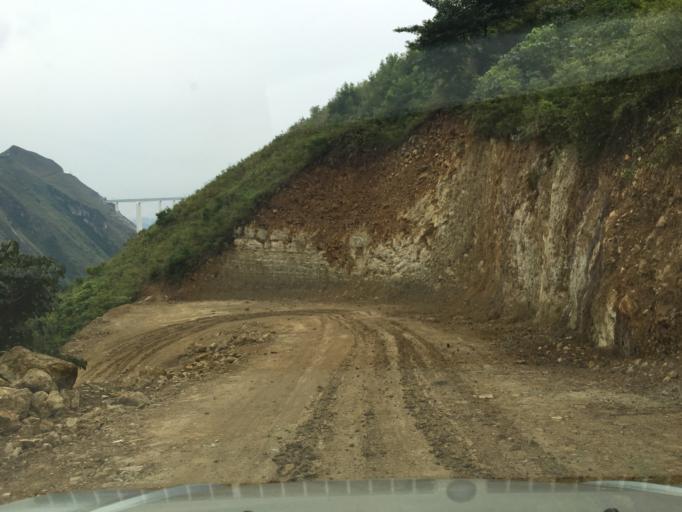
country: CN
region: Guizhou Sheng
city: Anshun
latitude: 25.9619
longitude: 105.2422
